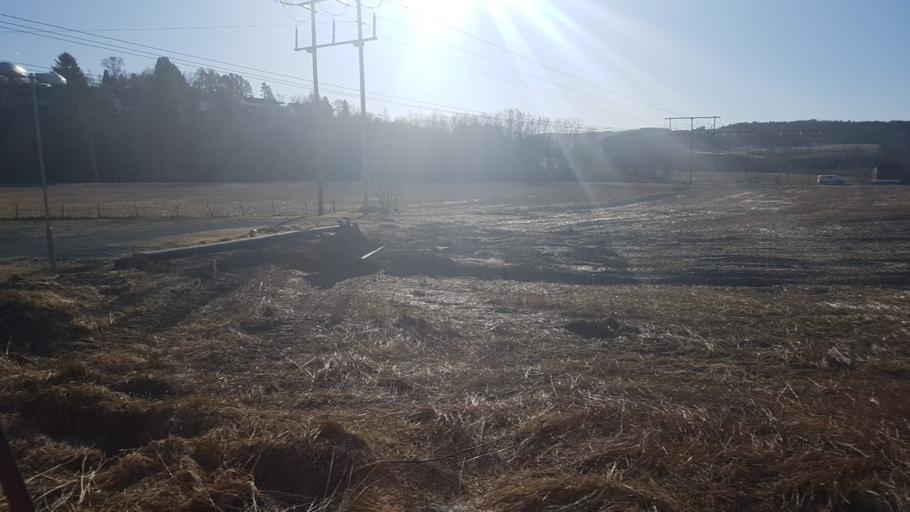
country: NO
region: Nord-Trondelag
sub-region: Levanger
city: Levanger
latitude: 63.7406
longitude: 11.2953
